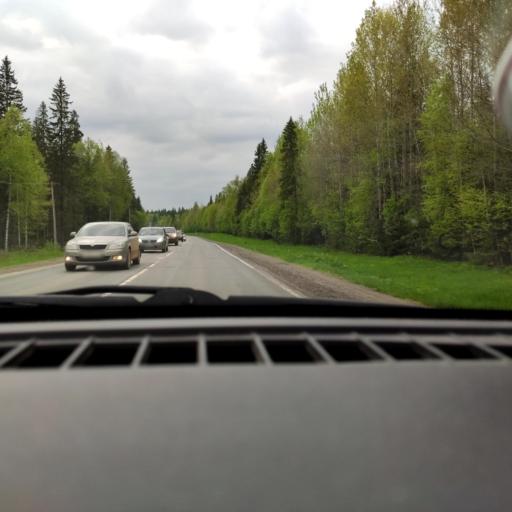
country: RU
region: Perm
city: Perm
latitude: 58.1984
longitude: 56.2077
